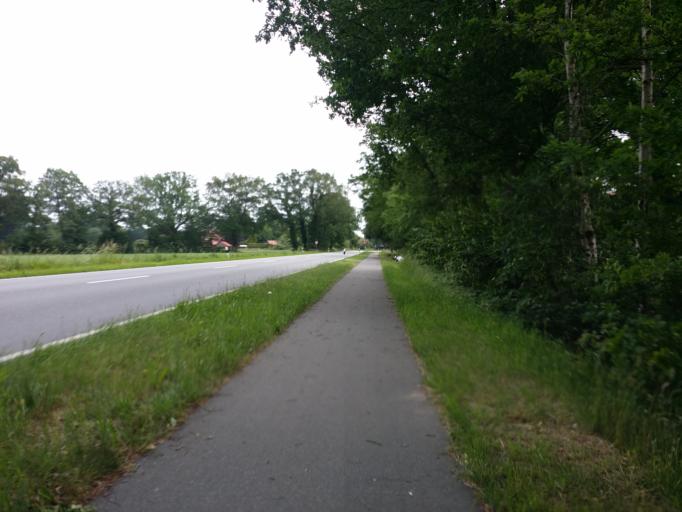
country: DE
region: Lower Saxony
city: Zetel
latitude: 53.3959
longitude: 7.9258
